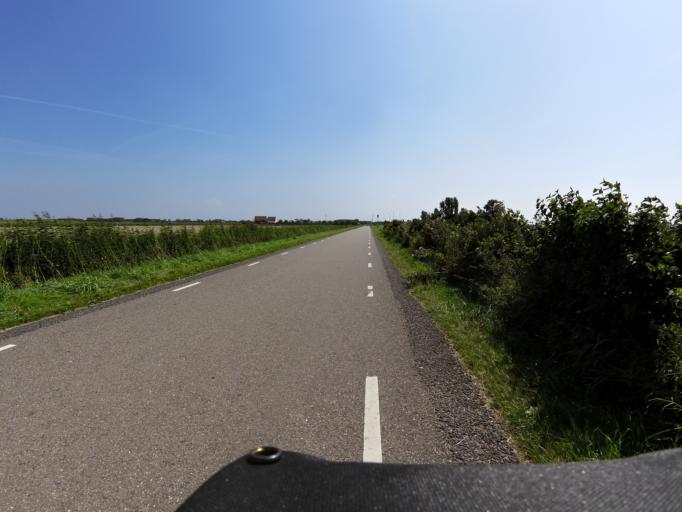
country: NL
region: South Holland
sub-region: Gemeente Goeree-Overflakkee
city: Middelharnis
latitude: 51.7319
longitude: 4.1700
